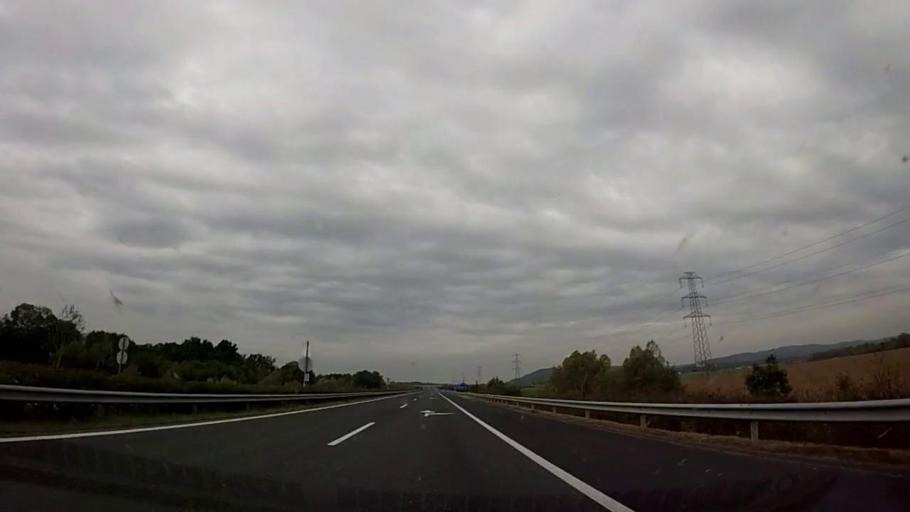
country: HR
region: Medimurska
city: Podturen
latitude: 46.5084
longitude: 16.5717
